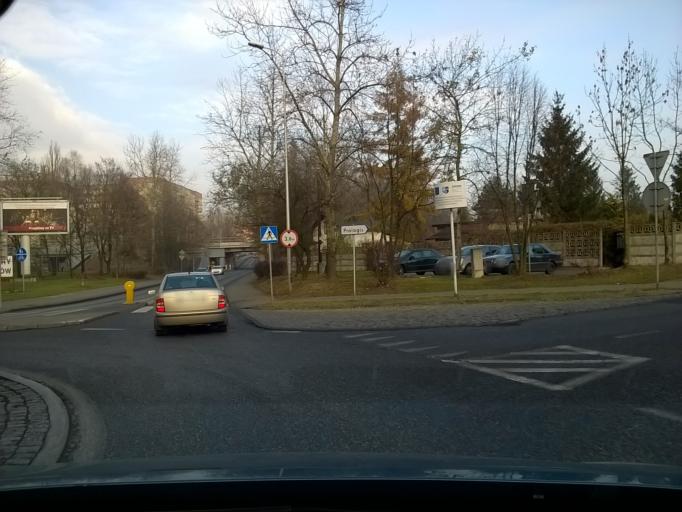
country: PL
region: Silesian Voivodeship
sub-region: Swietochlowice
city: Swietochlowice
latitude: 50.2587
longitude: 18.9360
